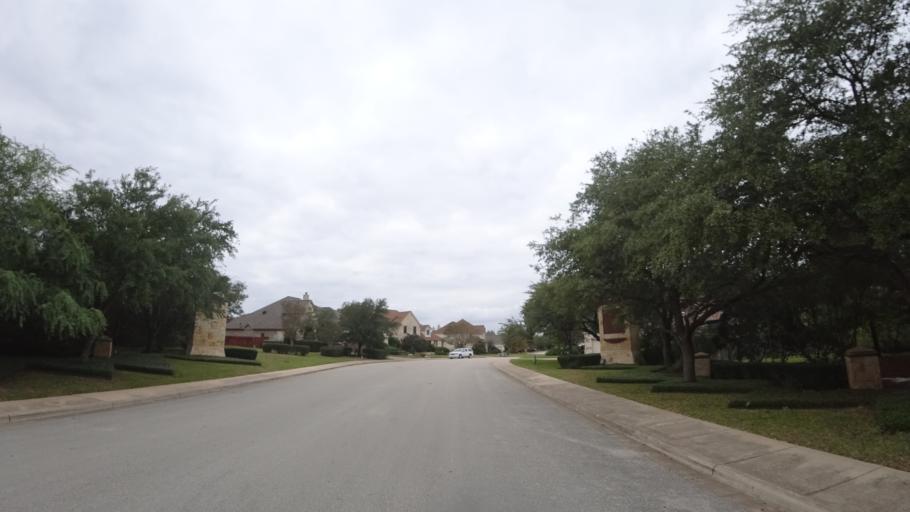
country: US
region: Texas
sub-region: Travis County
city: Bee Cave
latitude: 30.3113
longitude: -97.9250
